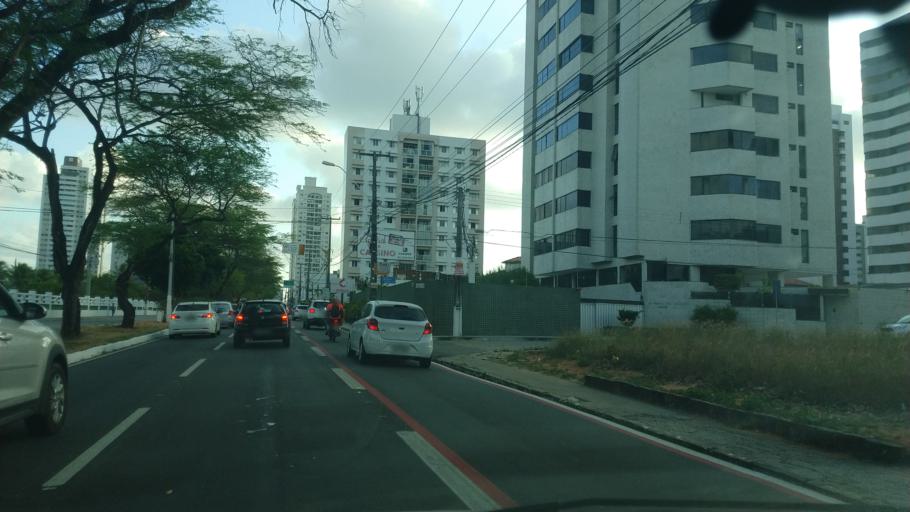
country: BR
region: Rio Grande do Norte
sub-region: Natal
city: Natal
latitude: -5.8039
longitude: -35.2019
